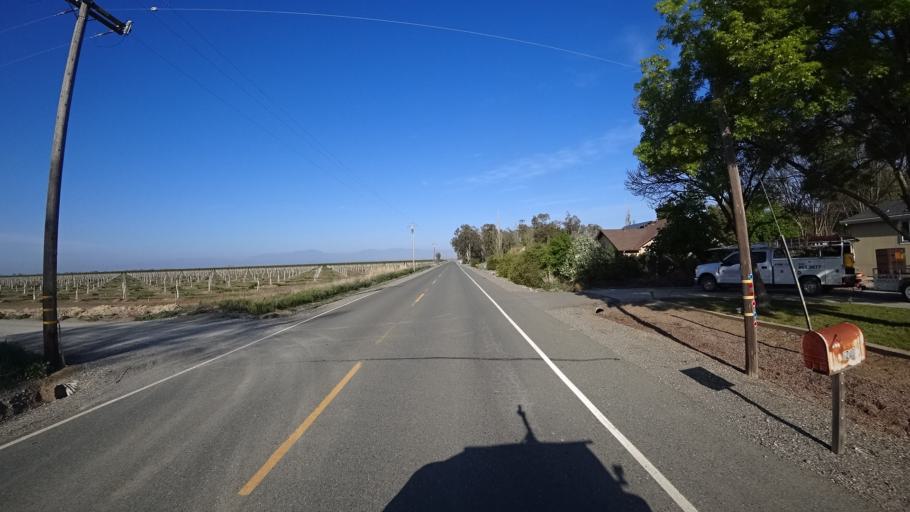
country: US
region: California
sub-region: Glenn County
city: Willows
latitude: 39.5824
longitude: -122.2217
